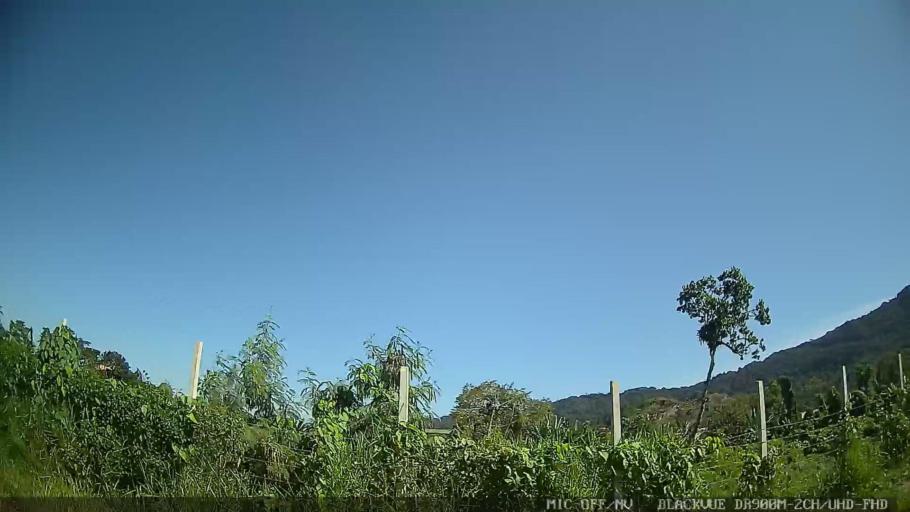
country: BR
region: Sao Paulo
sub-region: Guaruja
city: Guaruja
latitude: -23.9722
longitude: -46.2220
